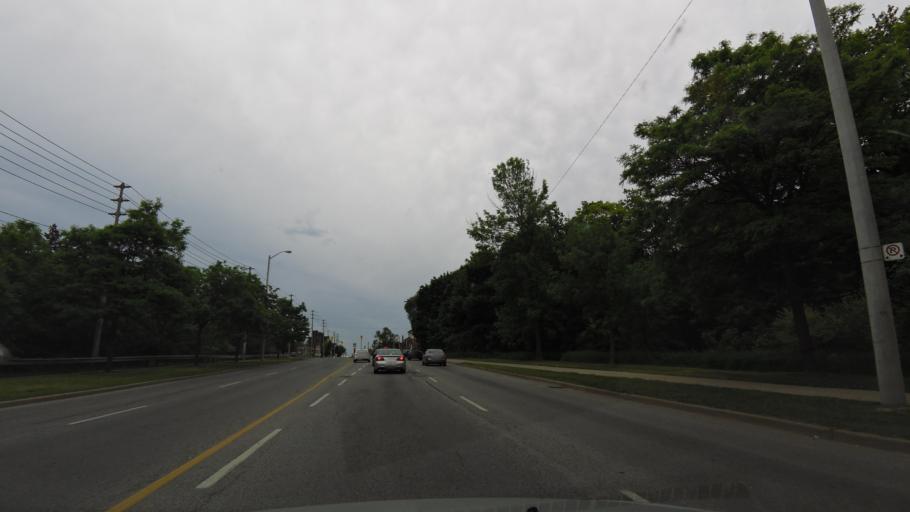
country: CA
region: Ontario
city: Etobicoke
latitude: 43.6824
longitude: -79.4982
